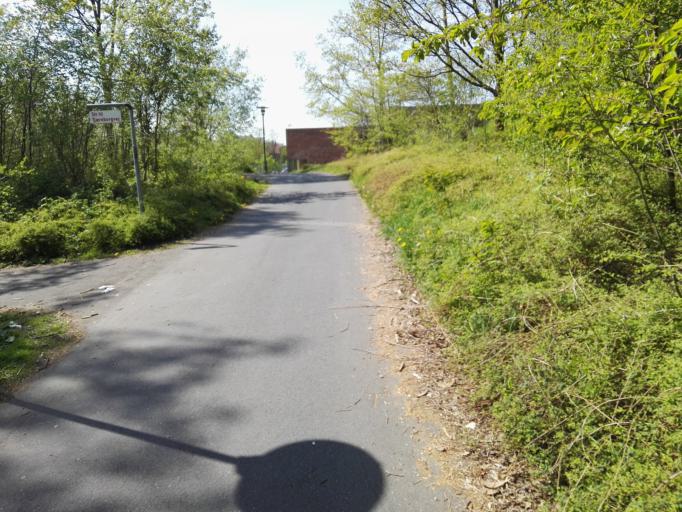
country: DK
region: Capital Region
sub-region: Ballerup Kommune
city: Malov
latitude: 55.7496
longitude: 12.3259
